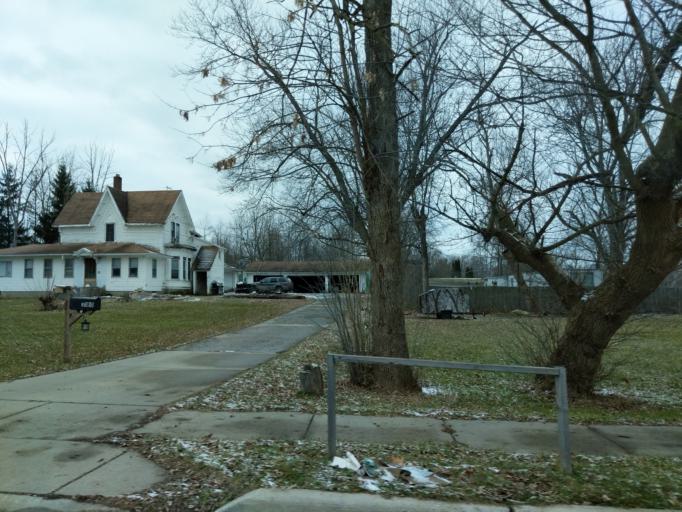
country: US
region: Michigan
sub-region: Sanilac County
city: Marlette
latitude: 43.3248
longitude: -83.0811
